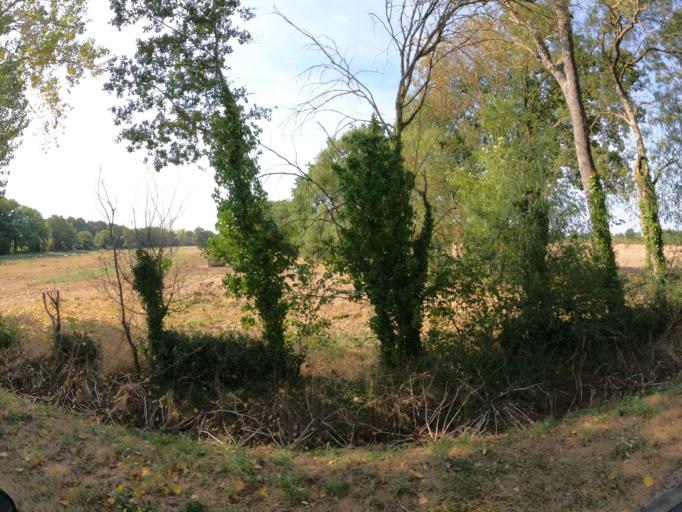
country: FR
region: Pays de la Loire
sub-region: Departement de la Vendee
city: Soullans
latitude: 46.8056
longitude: -1.8833
